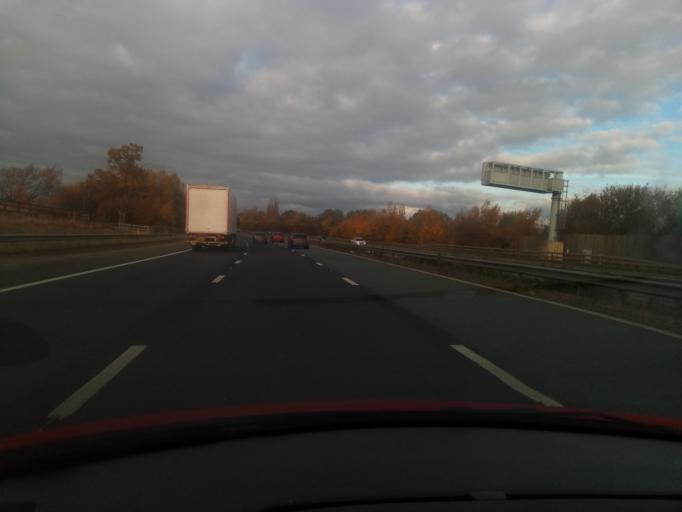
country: GB
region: England
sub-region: City and Borough of Leeds
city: Wetherby
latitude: 53.9776
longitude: -1.3640
